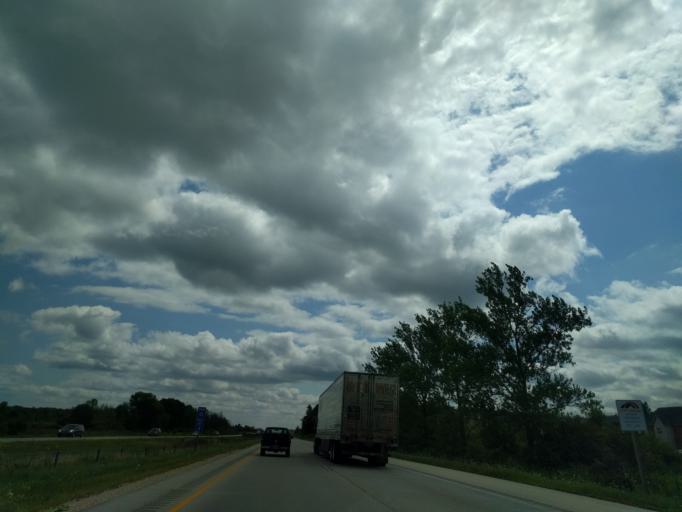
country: US
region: Wisconsin
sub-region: Ozaukee County
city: Thiensville
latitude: 43.2502
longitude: -87.9200
